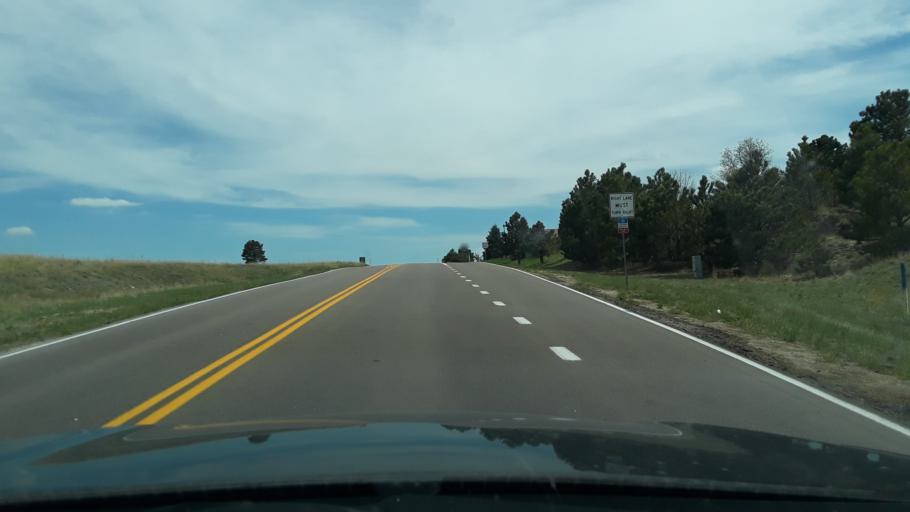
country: US
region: Colorado
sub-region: El Paso County
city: Monument
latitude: 39.0847
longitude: -104.8674
